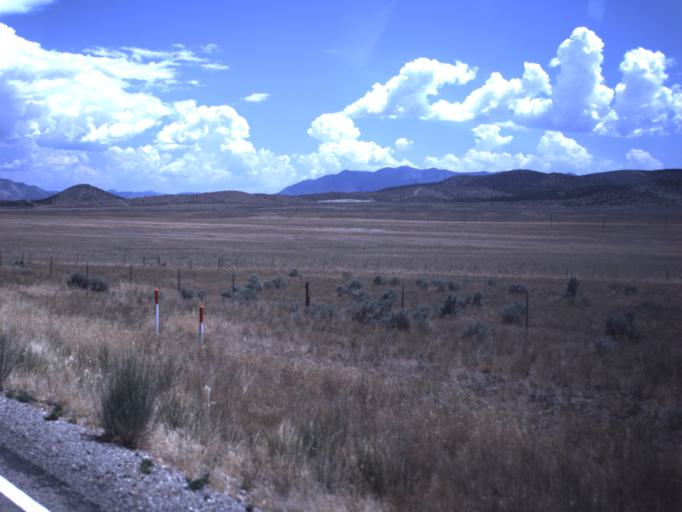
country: US
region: Utah
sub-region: Juab County
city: Nephi
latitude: 39.6707
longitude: -112.0302
